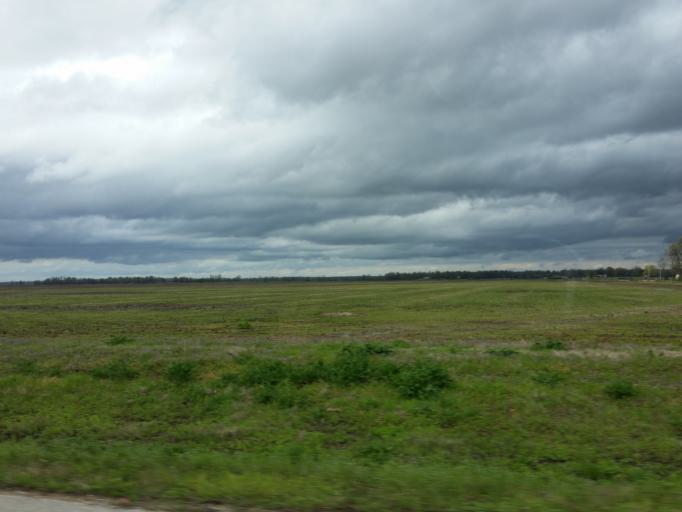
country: US
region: Missouri
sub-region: Butler County
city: Poplar Bluff
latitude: 36.6345
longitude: -90.5203
